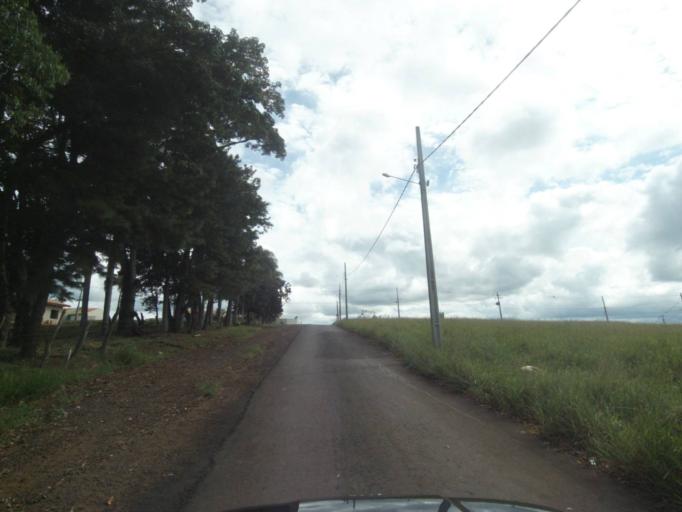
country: BR
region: Parana
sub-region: Telemaco Borba
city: Telemaco Borba
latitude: -24.3134
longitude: -50.6365
